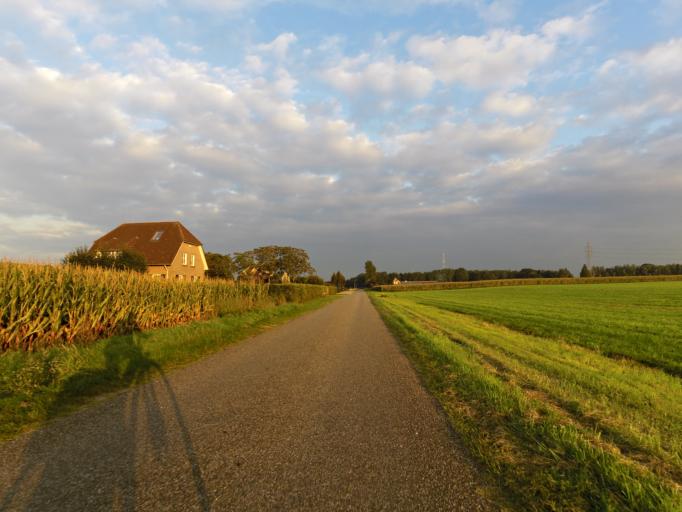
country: NL
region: Gelderland
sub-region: Gemeente Doesburg
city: Doesburg
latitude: 51.9411
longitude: 6.1751
